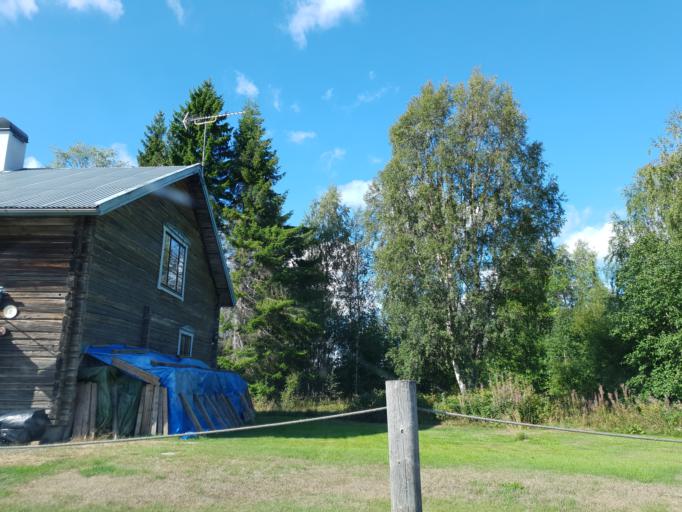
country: SE
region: Vaesterbotten
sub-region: Nordmalings Kommun
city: Nordmaling
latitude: 63.5364
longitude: 19.4003
